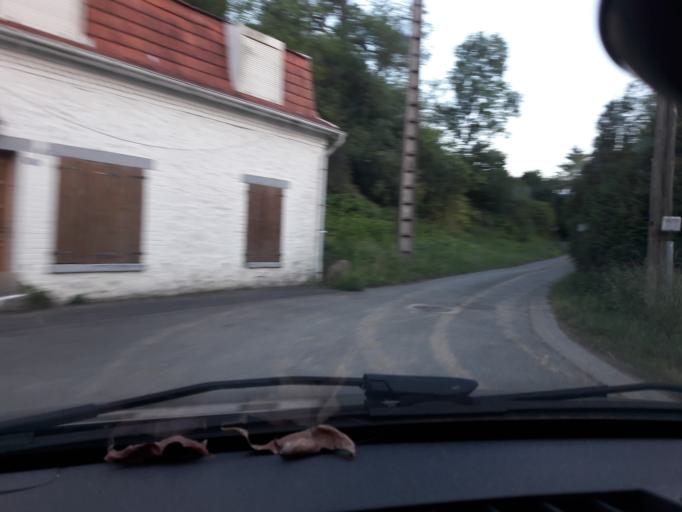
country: BE
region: Wallonia
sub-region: Province du Hainaut
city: Merbes-le-Chateau
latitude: 50.2647
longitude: 4.1812
